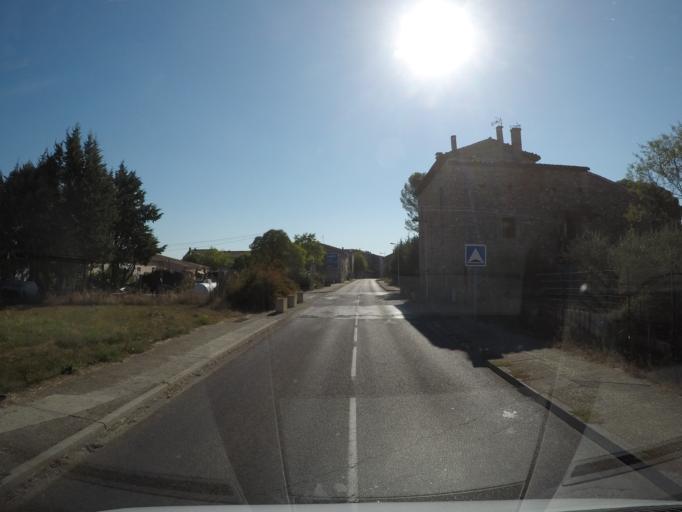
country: FR
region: Languedoc-Roussillon
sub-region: Departement du Gard
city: Boisset-et-Gaujac
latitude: 44.0272
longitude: 4.0208
